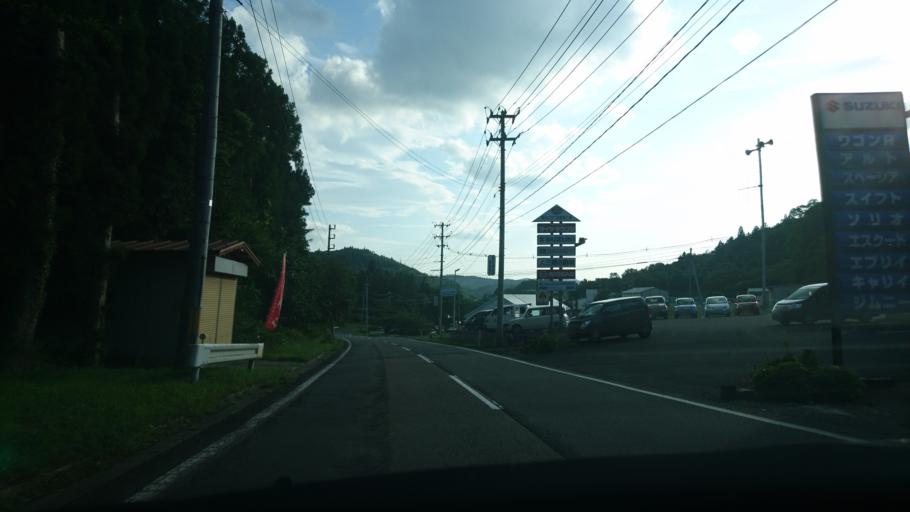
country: JP
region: Iwate
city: Ichinoseki
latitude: 38.9989
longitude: 141.2797
